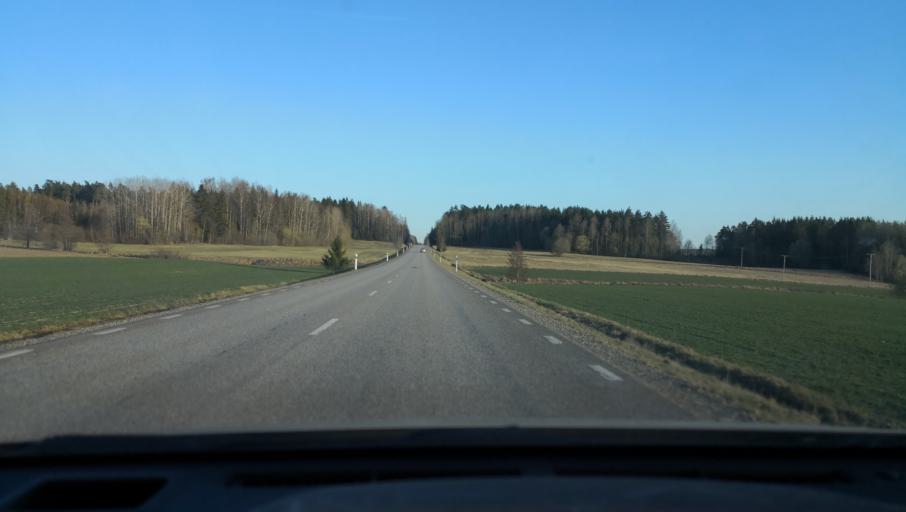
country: SE
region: Uppsala
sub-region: Heby Kommun
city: Heby
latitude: 59.9169
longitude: 16.8855
